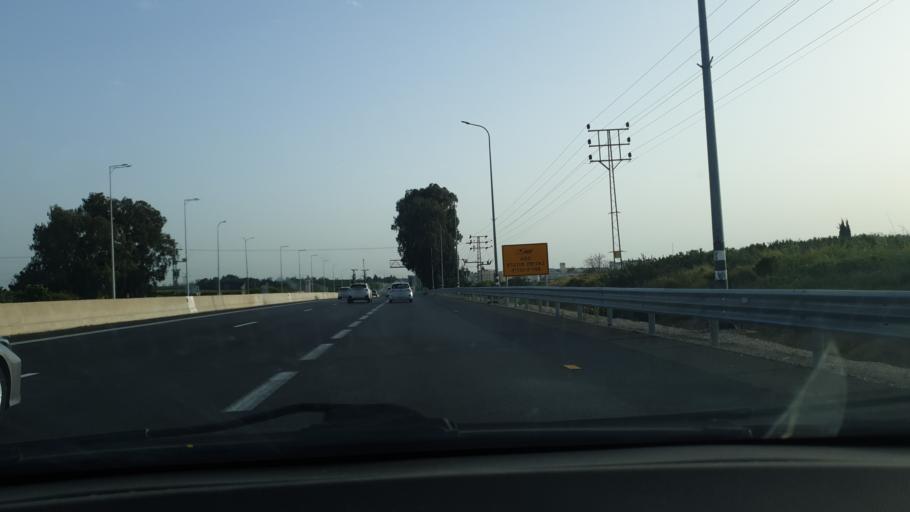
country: IL
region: Central District
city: Even Yehuda
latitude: 32.2477
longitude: 34.8889
